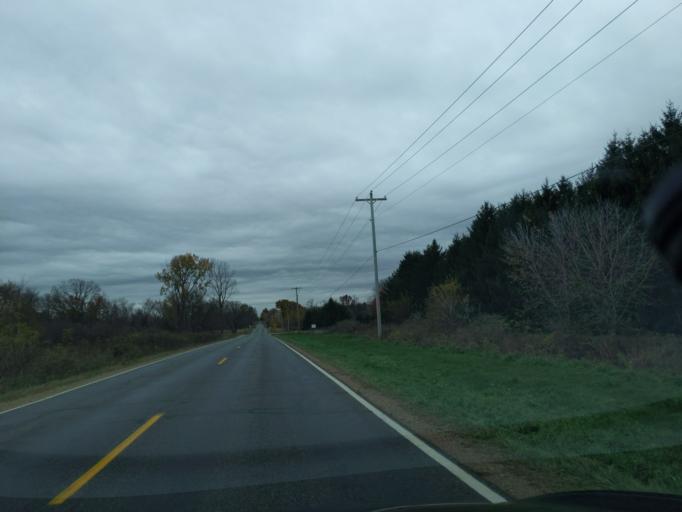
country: US
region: Michigan
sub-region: Jackson County
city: Spring Arbor
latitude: 42.2765
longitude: -84.6000
